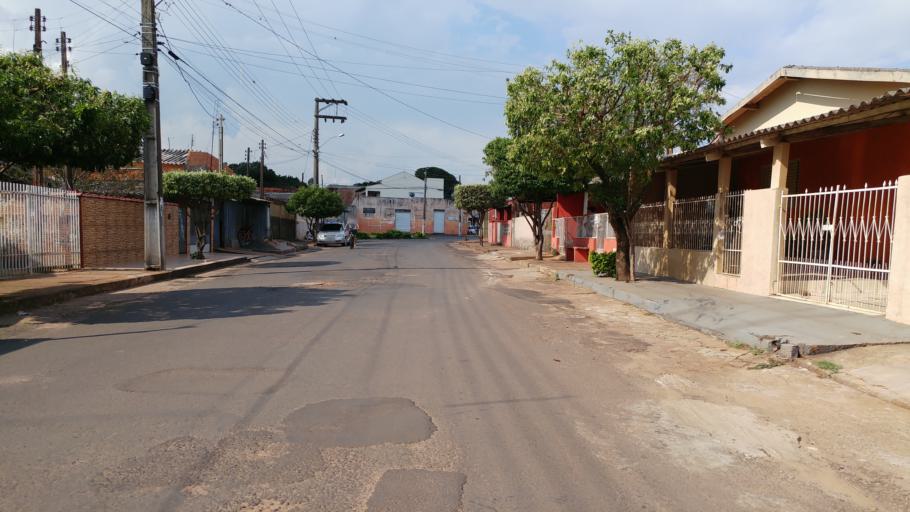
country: BR
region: Sao Paulo
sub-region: Paraguacu Paulista
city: Paraguacu Paulista
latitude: -22.4217
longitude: -50.5861
